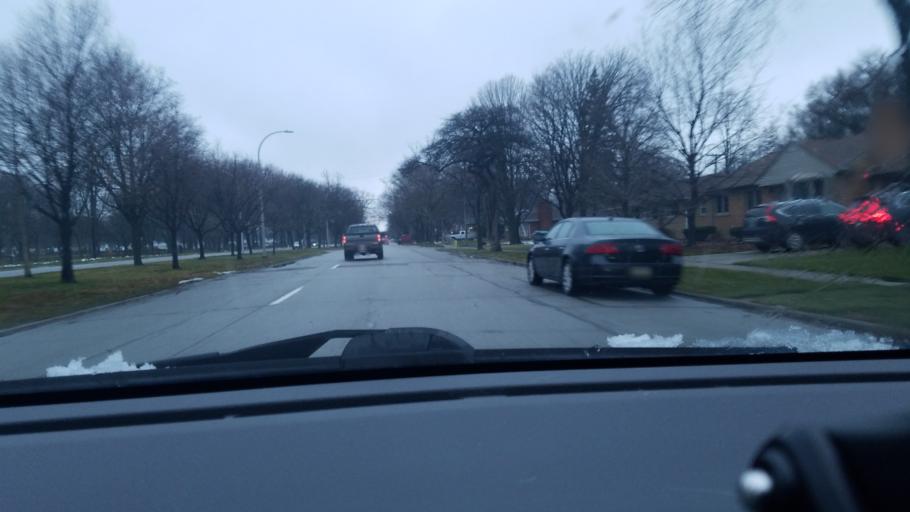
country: US
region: Michigan
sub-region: Wayne County
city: Allen Park
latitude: 42.2862
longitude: -83.2356
